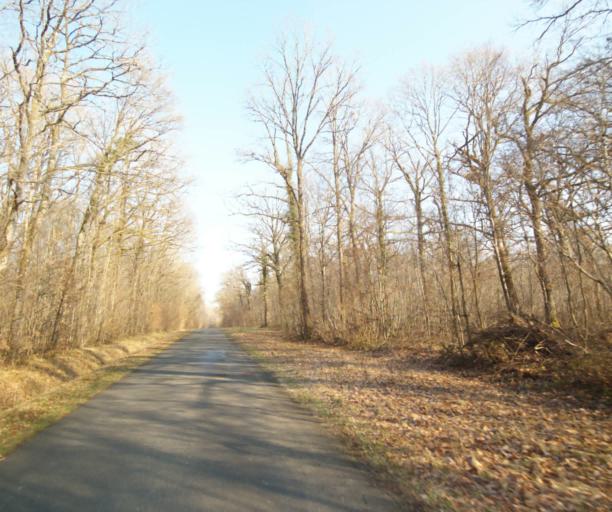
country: FR
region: Champagne-Ardenne
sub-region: Departement de la Haute-Marne
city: Wassy
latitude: 48.4621
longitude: 4.9406
